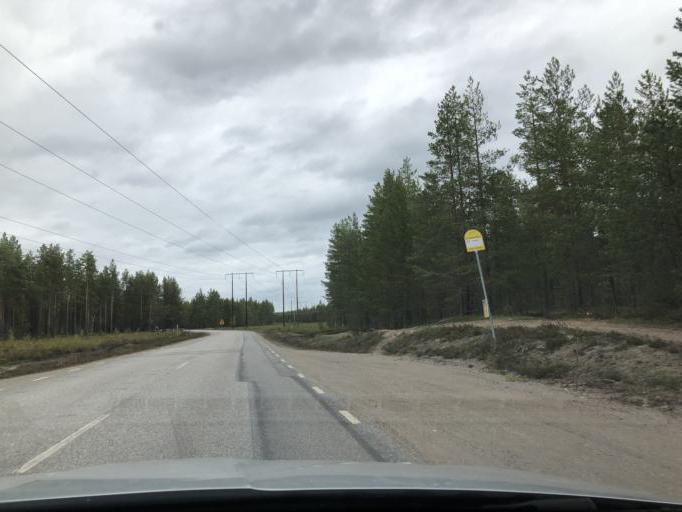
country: SE
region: Norrbotten
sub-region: Pitea Kommun
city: Pitea
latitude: 65.2393
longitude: 21.5212
